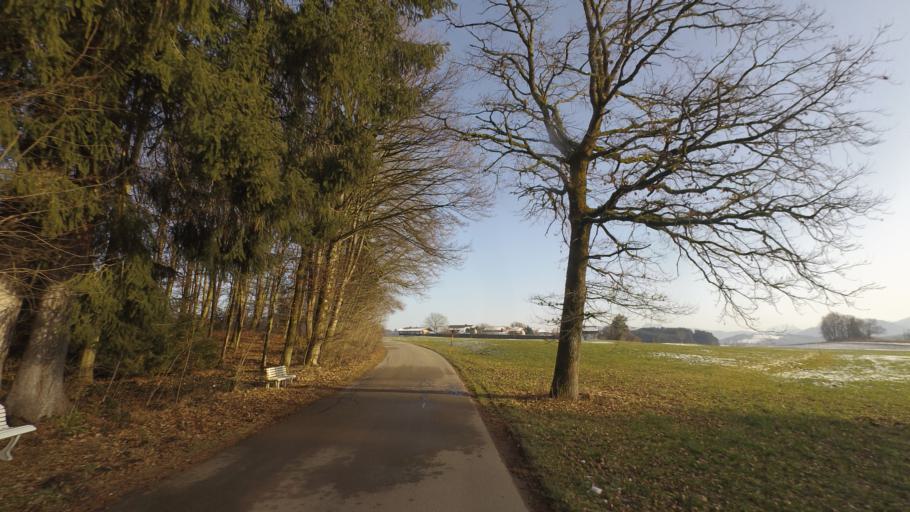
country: DE
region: Bavaria
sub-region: Upper Bavaria
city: Nussdorf
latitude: 47.8899
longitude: 12.6043
